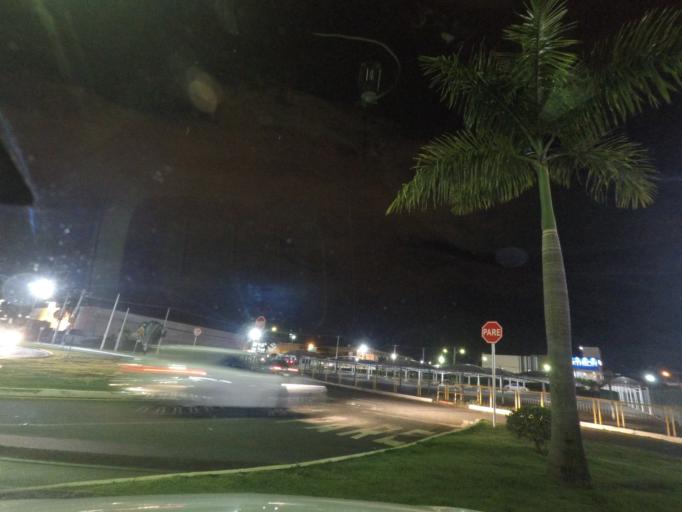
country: BR
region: Goias
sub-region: Goiania
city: Goiania
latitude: -16.7121
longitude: -49.2363
